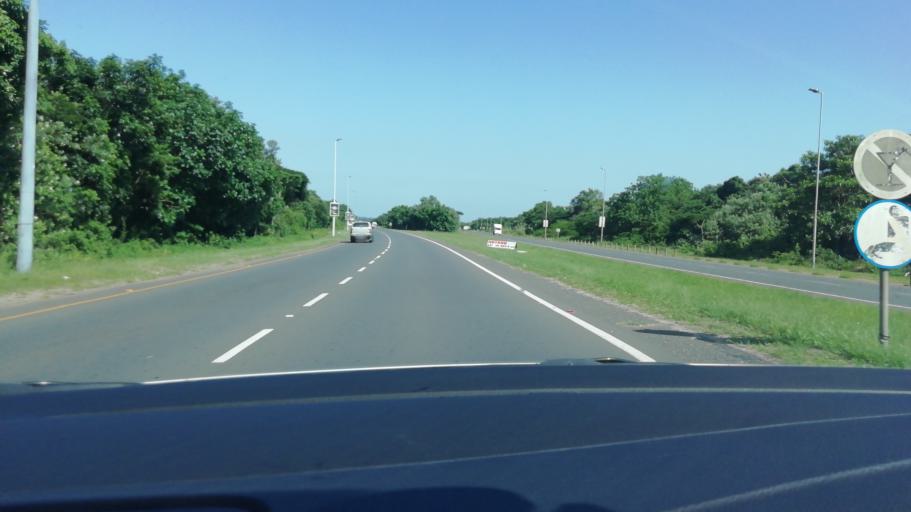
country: ZA
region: KwaZulu-Natal
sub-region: uThungulu District Municipality
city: Richards Bay
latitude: -28.7857
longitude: 32.0883
